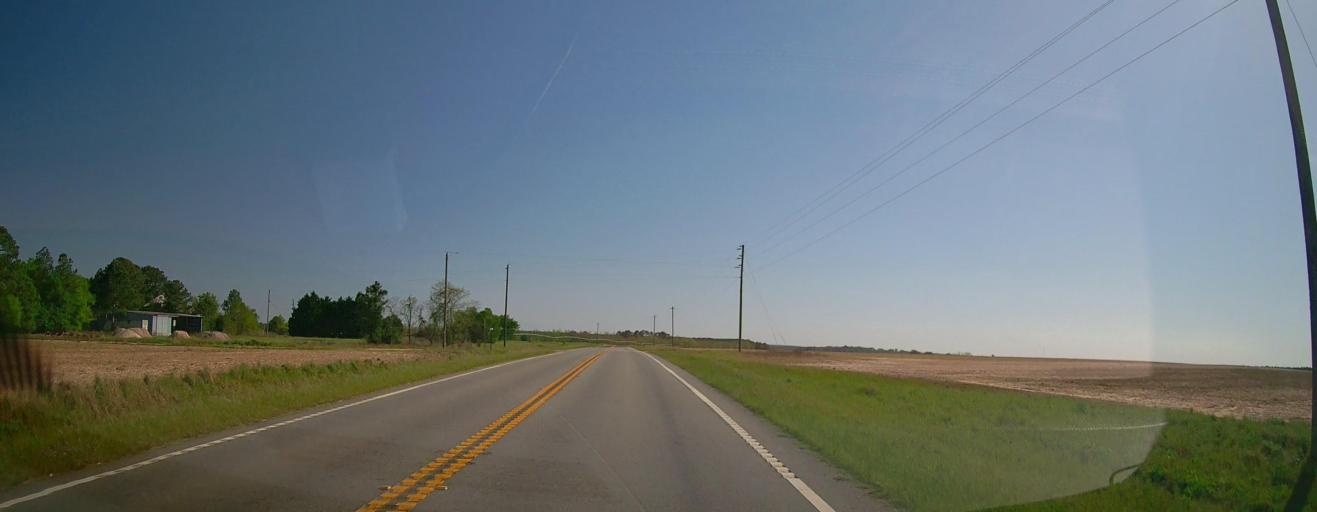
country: US
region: Georgia
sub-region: Pulaski County
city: Hawkinsville
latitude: 32.1839
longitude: -83.5044
